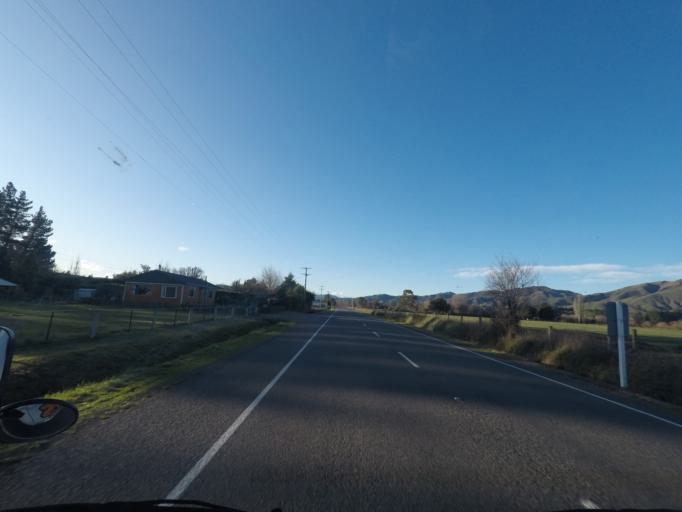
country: NZ
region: Canterbury
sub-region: Kaikoura District
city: Kaikoura
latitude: -42.7154
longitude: 173.2891
